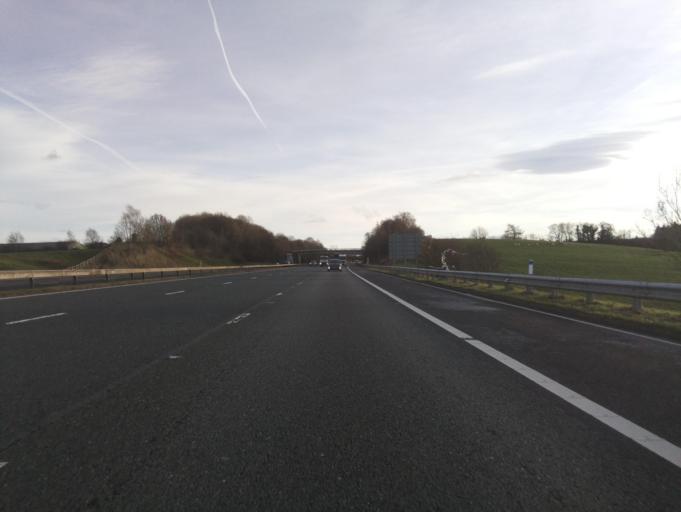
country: GB
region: England
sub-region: Cumbria
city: Penrith
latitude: 54.6389
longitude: -2.7320
